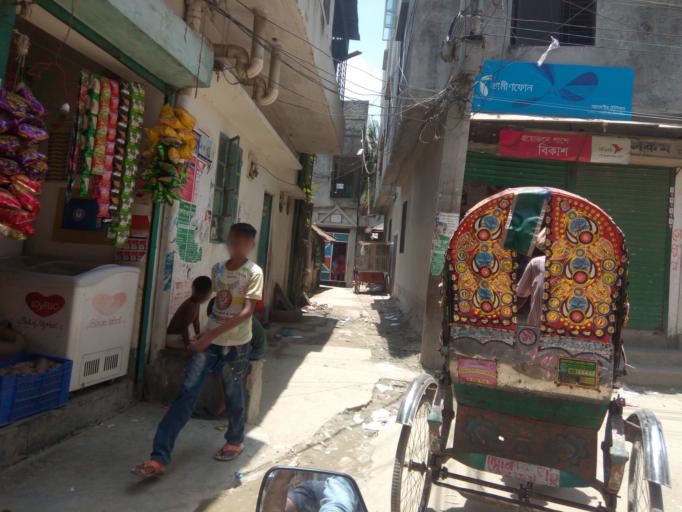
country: BD
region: Dhaka
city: Paltan
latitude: 23.7562
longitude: 90.4352
